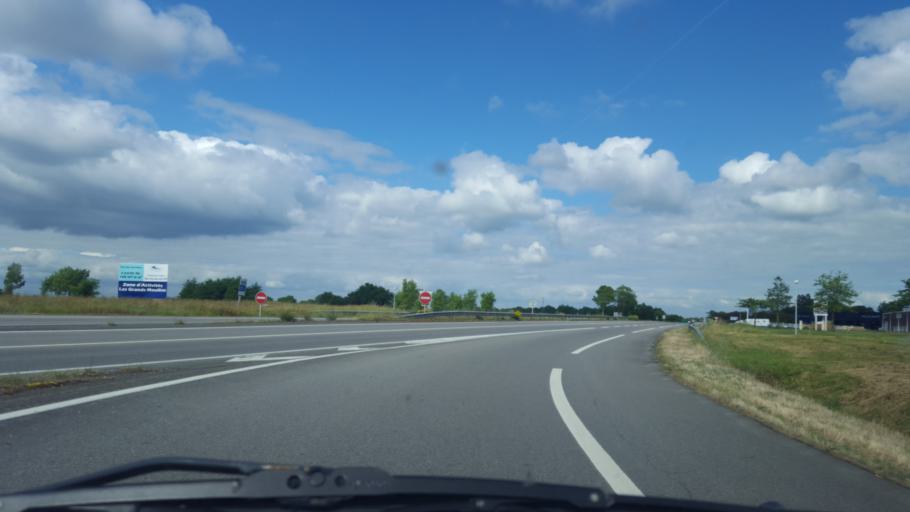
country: FR
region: Pays de la Loire
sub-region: Departement de la Loire-Atlantique
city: Paulx
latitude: 46.9986
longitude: -1.7386
